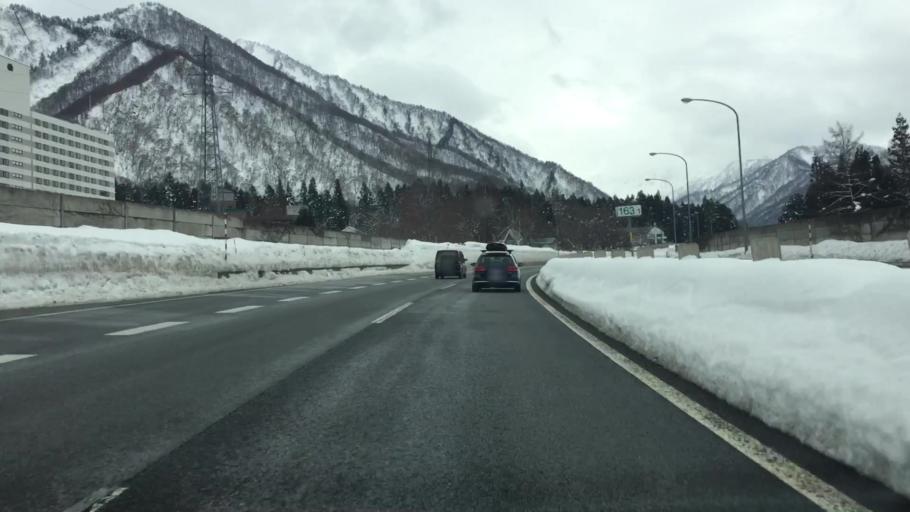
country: JP
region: Niigata
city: Shiozawa
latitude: 36.9054
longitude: 138.8465
